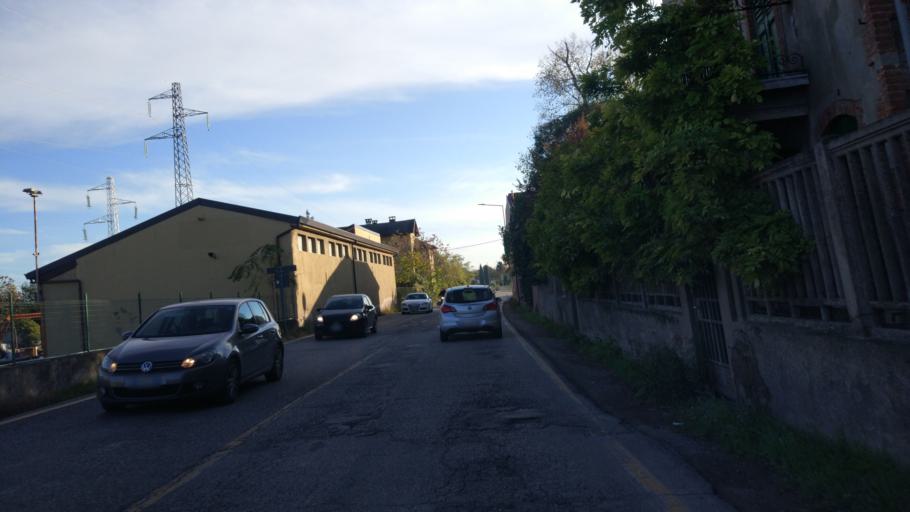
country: IT
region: Veneto
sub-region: Provincia di Verona
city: Volargne
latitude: 45.5215
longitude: 10.8188
